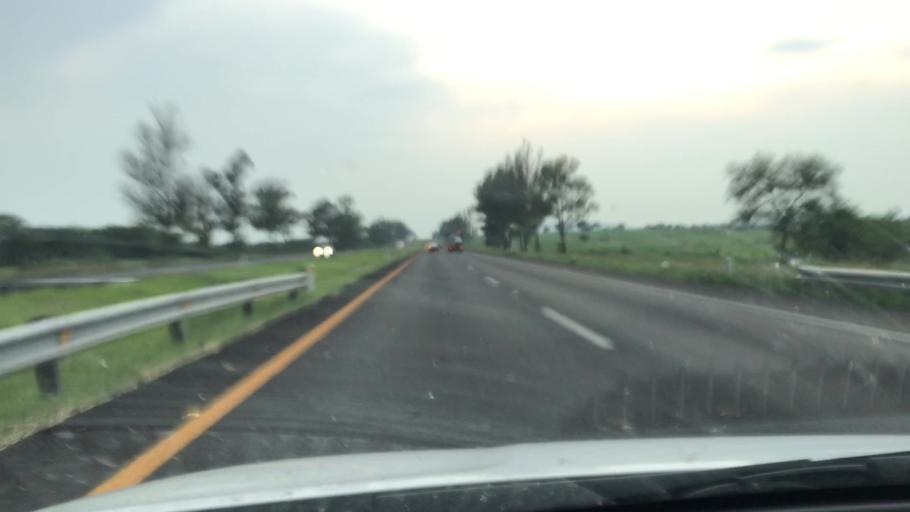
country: MX
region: Jalisco
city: Jamay
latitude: 20.3572
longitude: -102.6408
